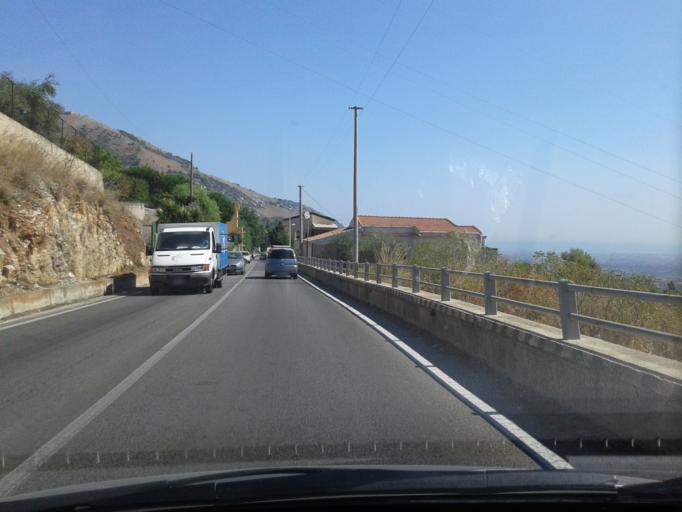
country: IT
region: Sicily
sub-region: Palermo
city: Cannizzaro-Favara
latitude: 38.0633
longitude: 13.2654
